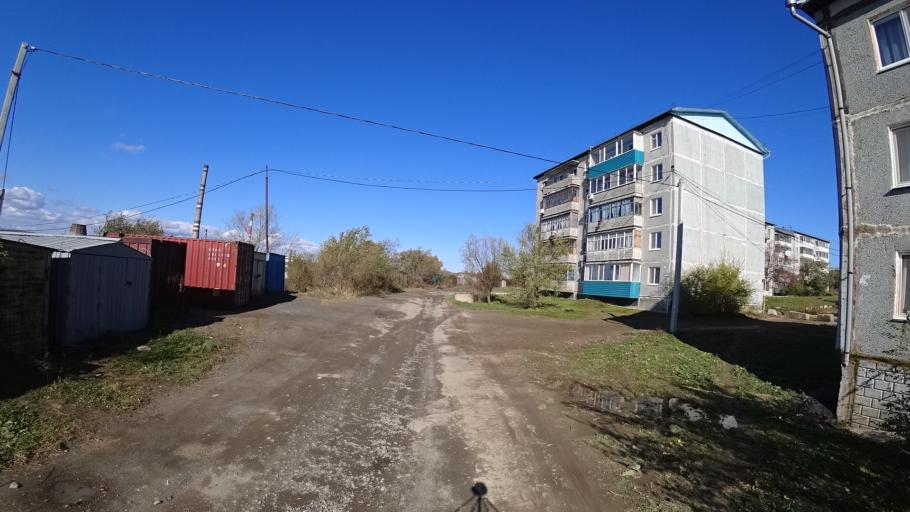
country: RU
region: Khabarovsk Krai
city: Amursk
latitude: 50.2168
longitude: 136.8892
